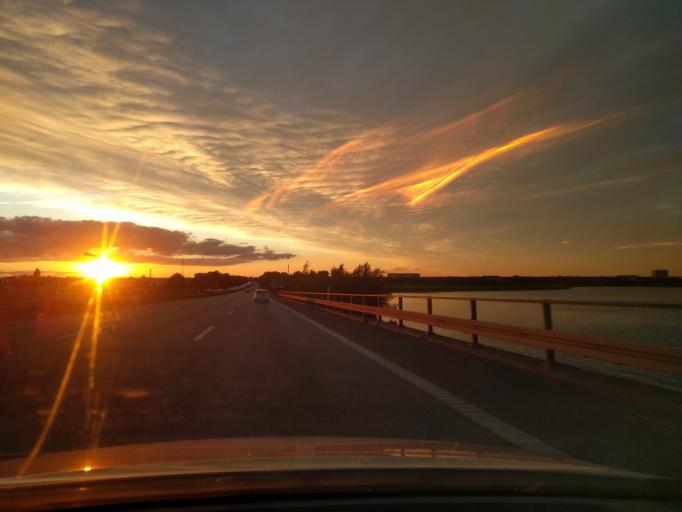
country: DK
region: Capital Region
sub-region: Hvidovre Kommune
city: Hvidovre
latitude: 55.6147
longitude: 12.5059
